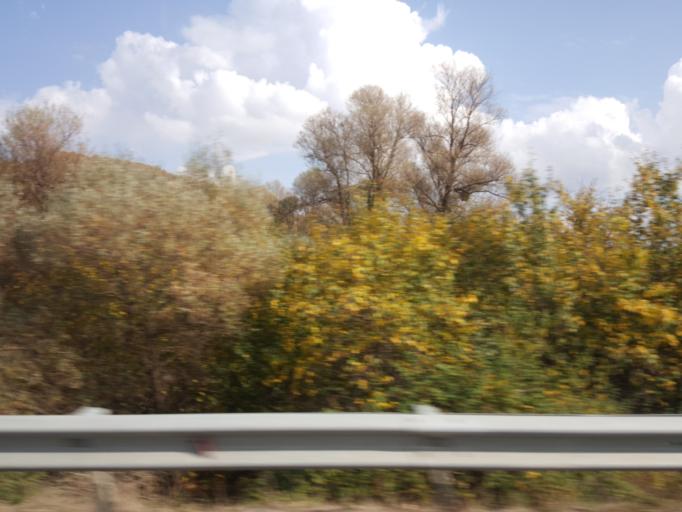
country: TR
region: Corum
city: Alaca
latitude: 40.3042
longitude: 34.6553
